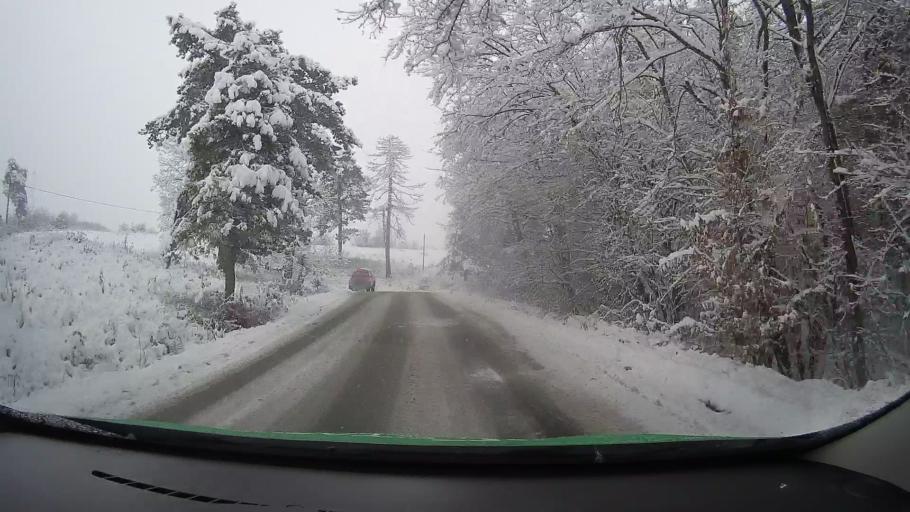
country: RO
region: Hunedoara
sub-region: Comuna Teliucu Inferior
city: Teliucu Inferior
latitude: 45.7057
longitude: 22.8820
